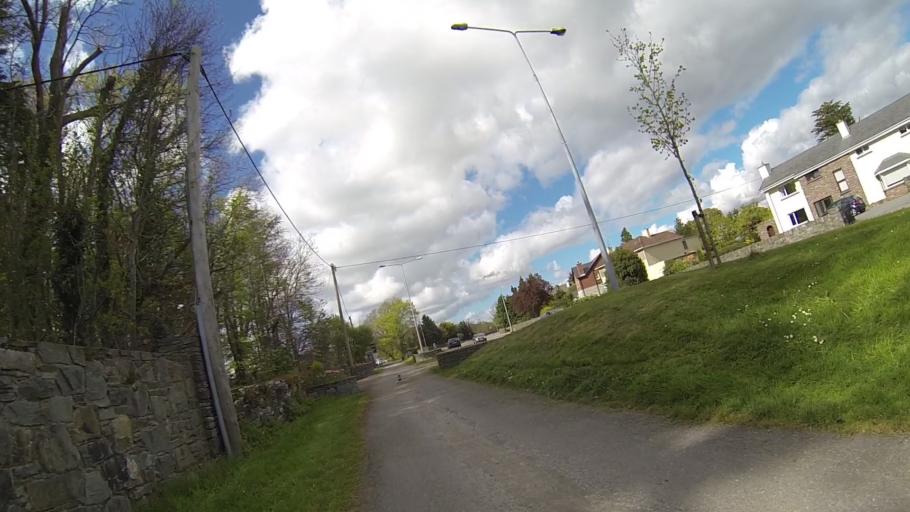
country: IE
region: Munster
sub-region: Ciarrai
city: Cill Airne
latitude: 52.0464
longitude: -9.5056
